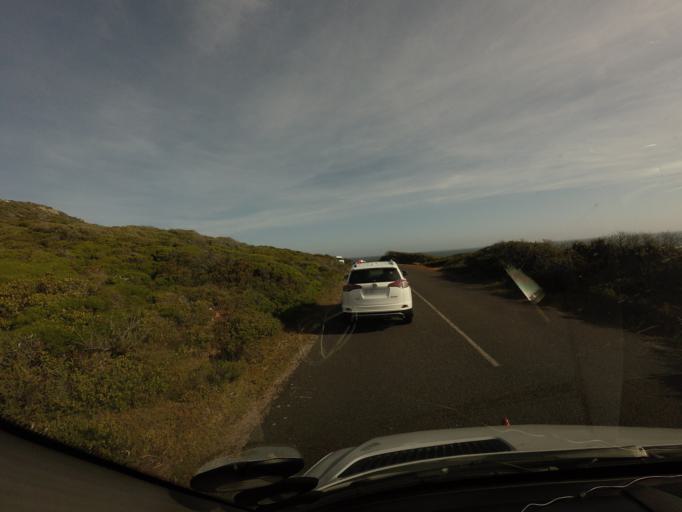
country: ZA
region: Western Cape
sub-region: City of Cape Town
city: Retreat
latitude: -34.3418
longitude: 18.4606
